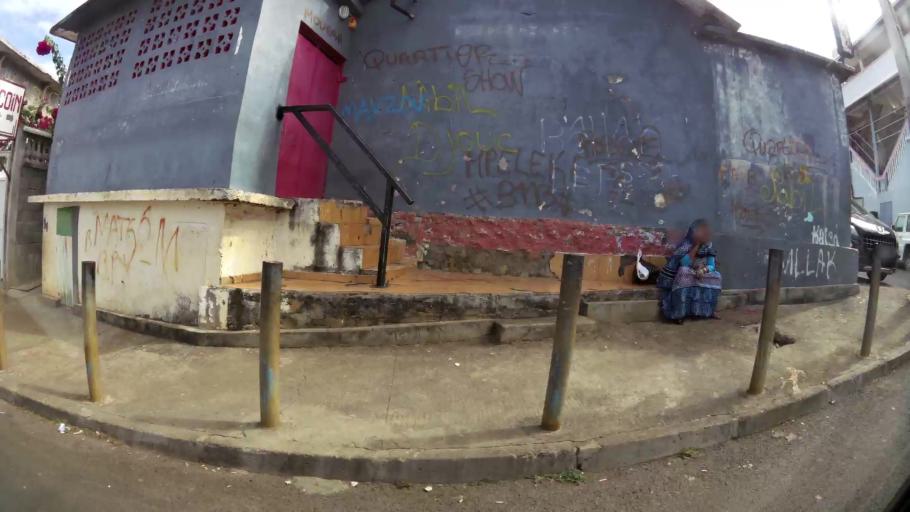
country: YT
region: Mamoudzou
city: Mamoudzou
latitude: -12.7808
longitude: 45.2290
